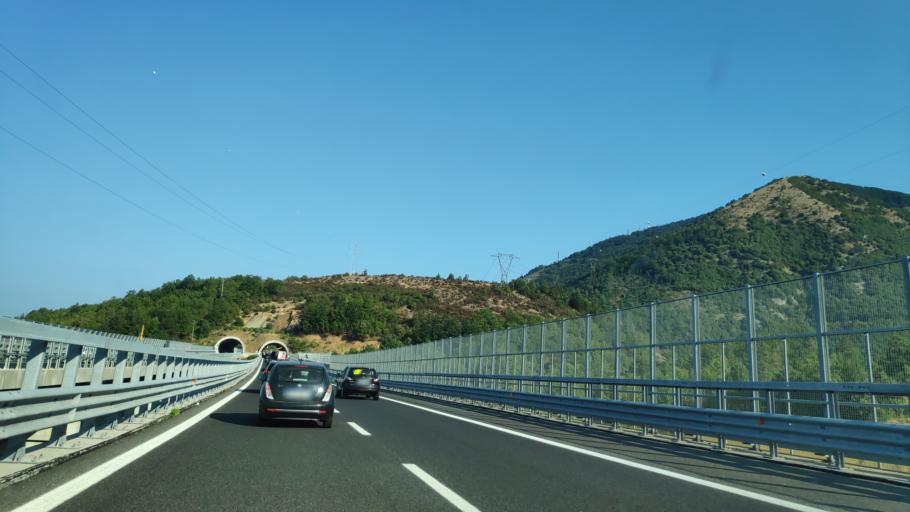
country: IT
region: Basilicate
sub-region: Provincia di Potenza
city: Lagonegro
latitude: 40.1237
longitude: 15.7816
